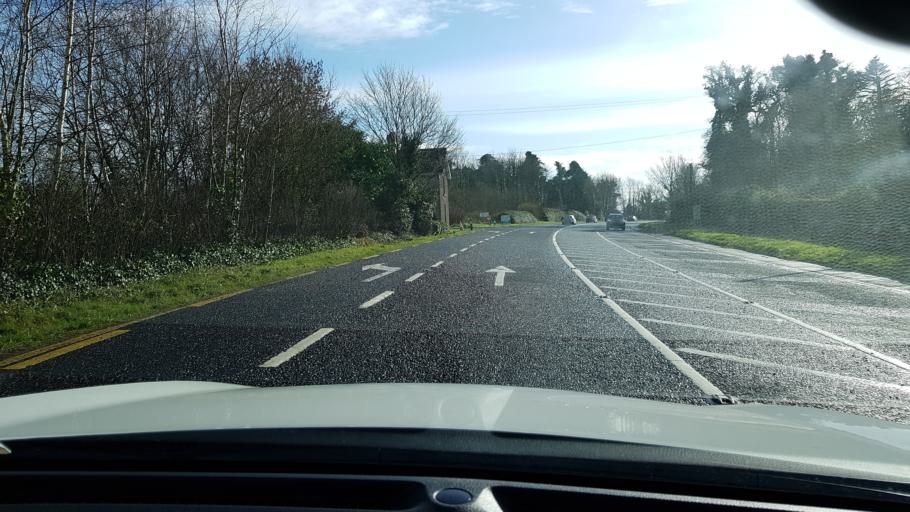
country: IE
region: Leinster
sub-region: An Longfort
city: Longford
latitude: 53.7828
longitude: -7.8372
